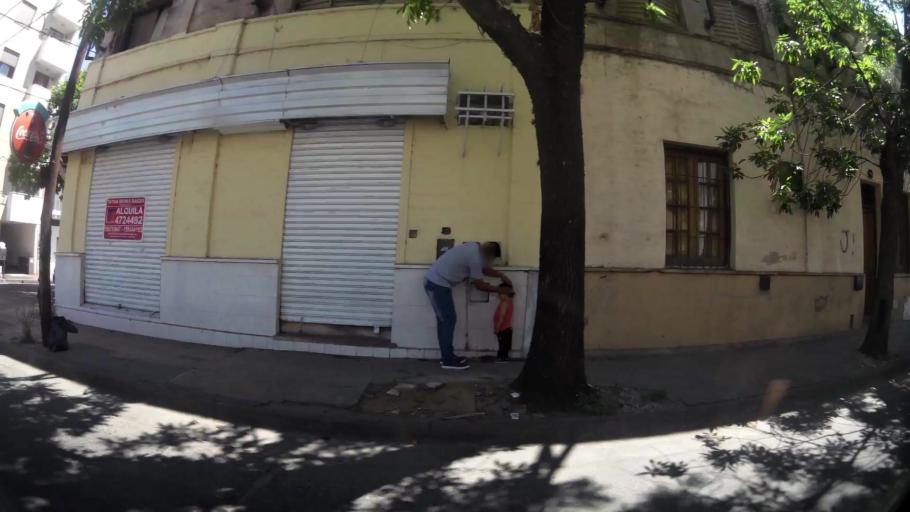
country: AR
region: Cordoba
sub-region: Departamento de Capital
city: Cordoba
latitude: -31.4026
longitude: -64.1942
